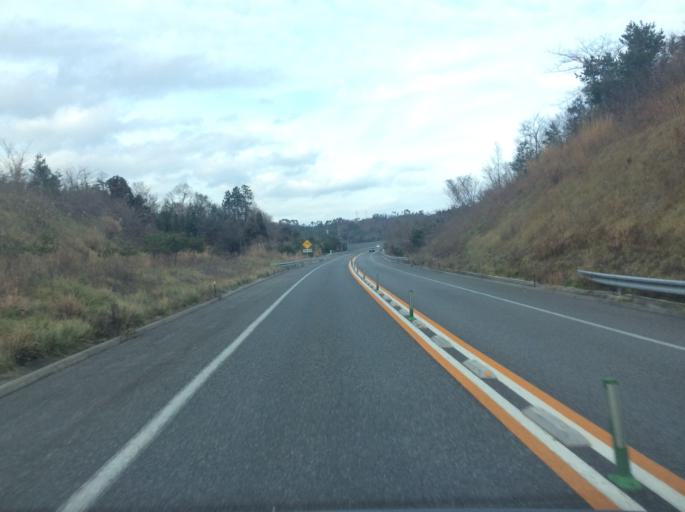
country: JP
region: Fukushima
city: Iwaki
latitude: 37.1637
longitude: 140.9666
